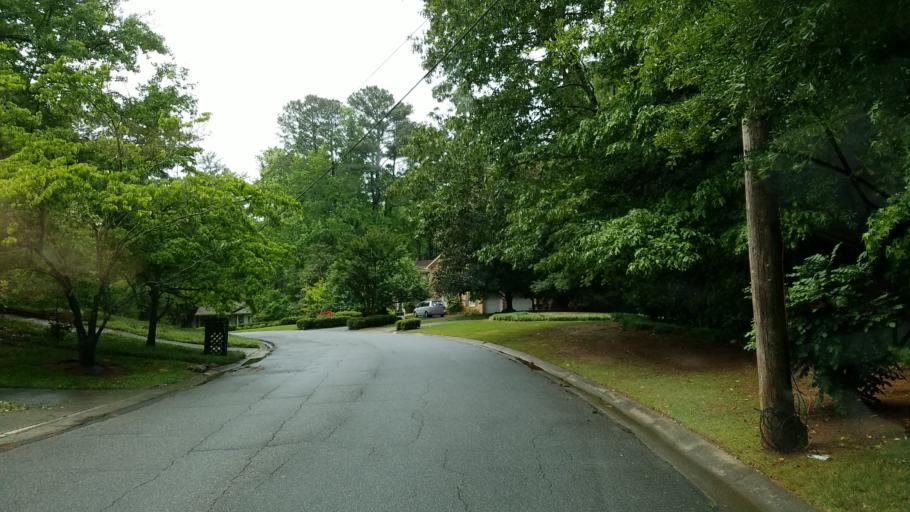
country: US
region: Georgia
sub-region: DeKalb County
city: Dunwoody
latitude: 33.9587
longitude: -84.3493
